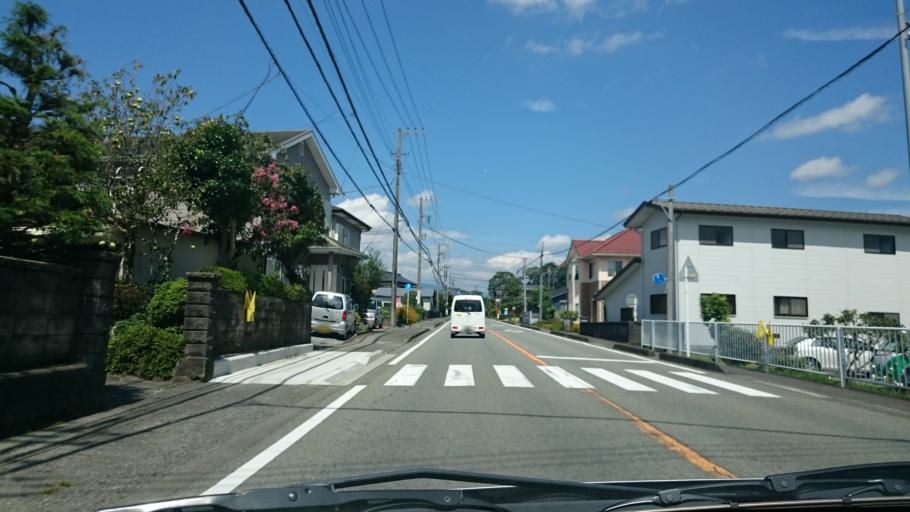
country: JP
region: Shizuoka
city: Gotemba
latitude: 35.2611
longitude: 138.9232
